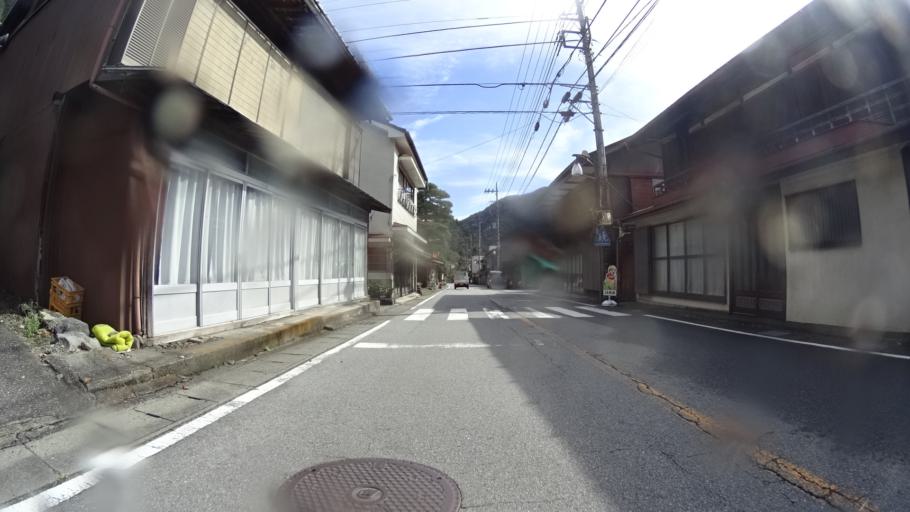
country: JP
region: Yamanashi
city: Otsuki
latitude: 35.7913
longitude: 138.9185
